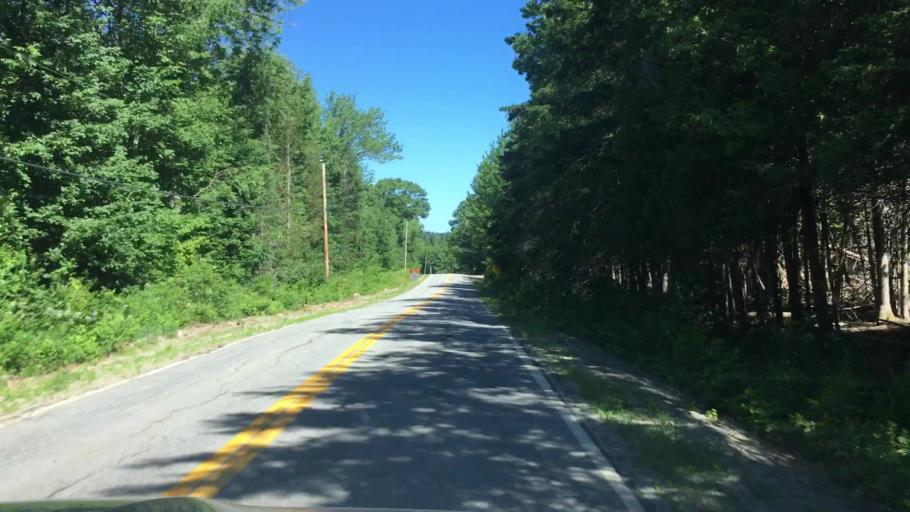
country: US
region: Maine
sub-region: Hancock County
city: Penobscot
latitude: 44.4211
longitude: -68.7056
